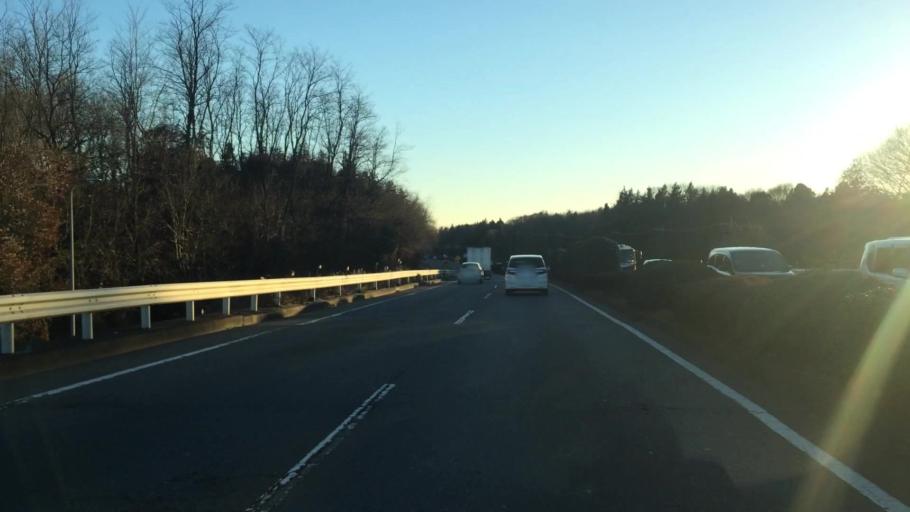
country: JP
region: Tochigi
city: Utsunomiya-shi
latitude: 36.5222
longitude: 139.9207
